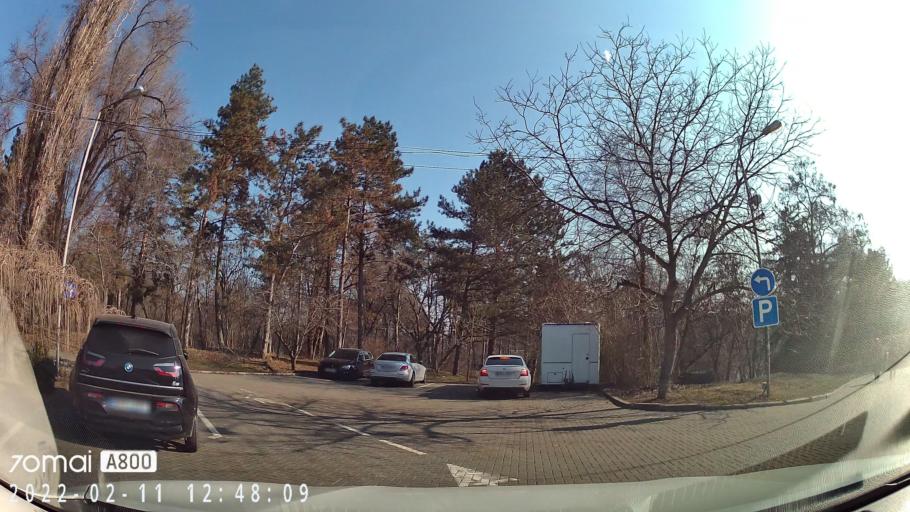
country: MD
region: Chisinau
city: Chisinau
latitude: 47.0028
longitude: 28.8484
